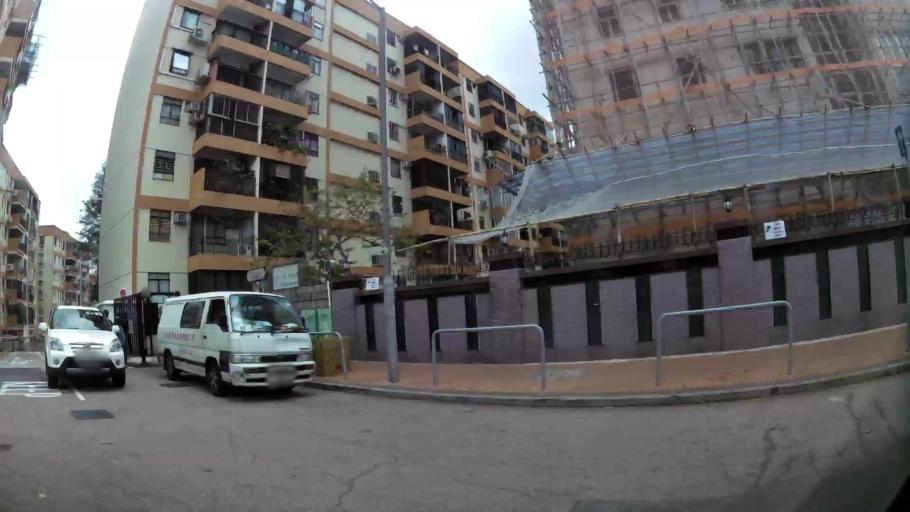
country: HK
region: Wong Tai Sin
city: Wong Tai Sin
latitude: 22.3423
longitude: 114.1805
